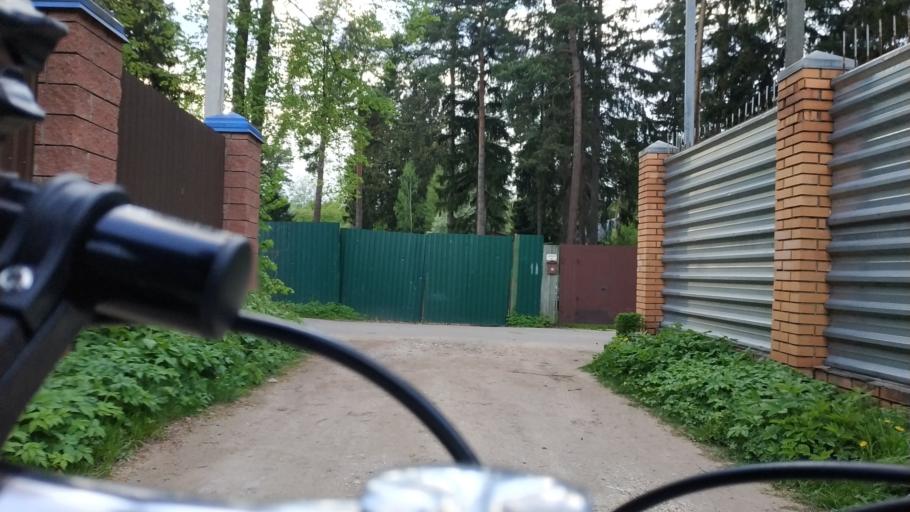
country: RU
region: Moskovskaya
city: Kratovo
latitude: 55.5958
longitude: 38.1640
